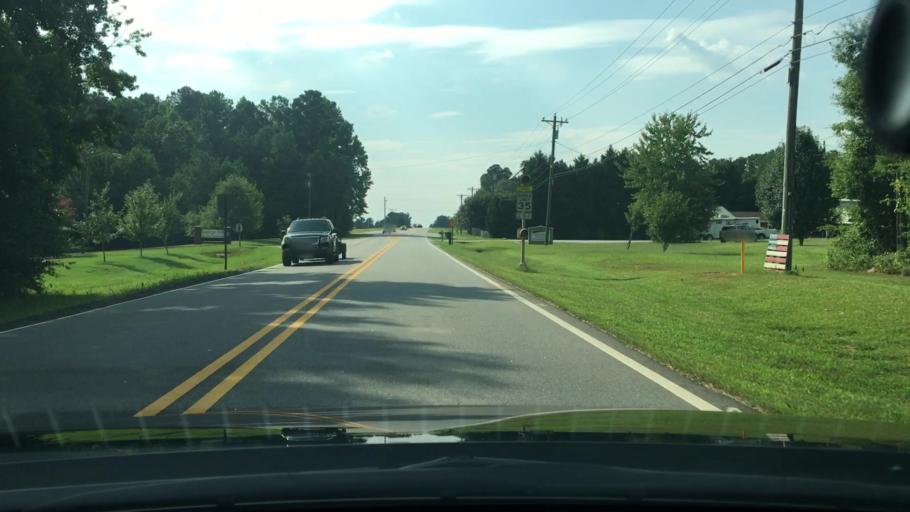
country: US
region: Georgia
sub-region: Coweta County
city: East Newnan
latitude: 33.3411
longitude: -84.6862
